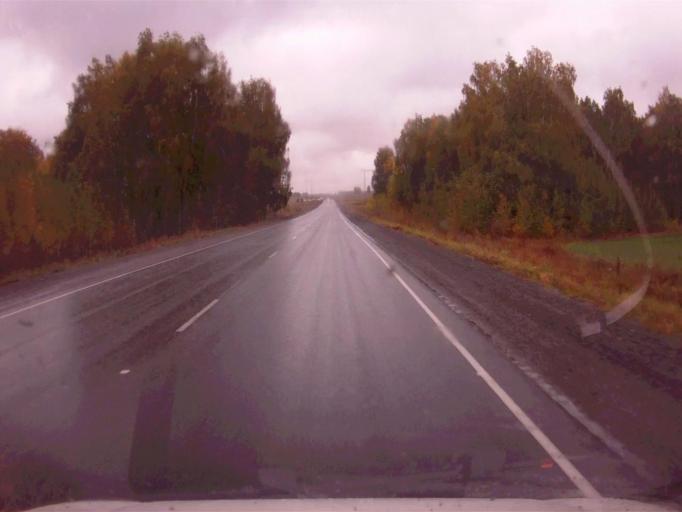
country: RU
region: Chelyabinsk
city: Roshchino
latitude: 55.3873
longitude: 61.1293
